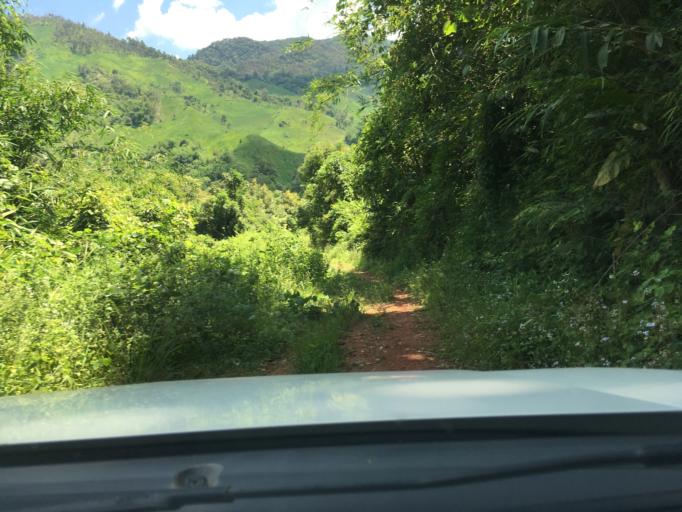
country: LA
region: Phongsali
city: Phongsali
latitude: 21.7896
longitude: 101.8653
